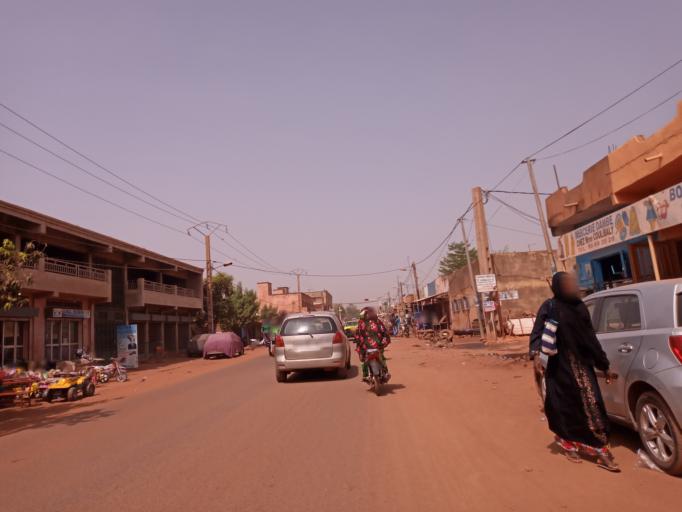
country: ML
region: Bamako
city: Bamako
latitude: 12.5888
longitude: -7.9812
